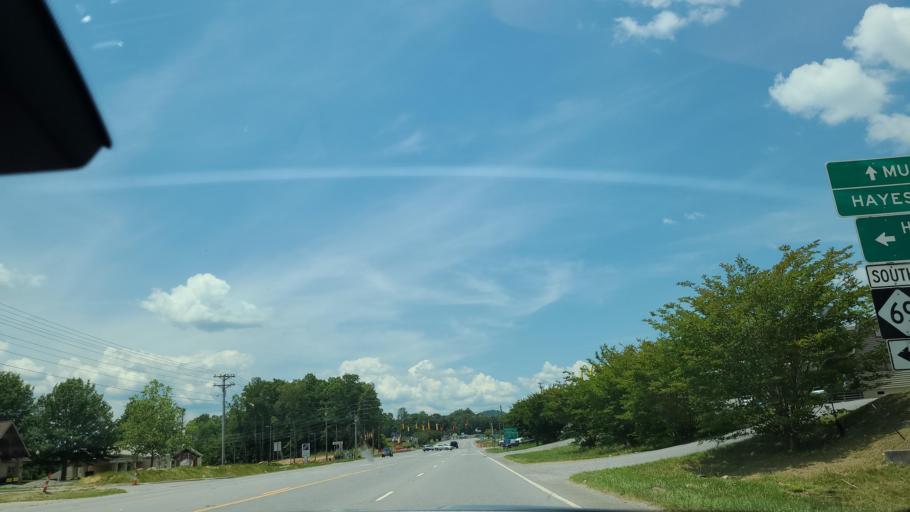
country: US
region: North Carolina
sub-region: Clay County
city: Hayesville
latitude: 35.0347
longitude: -83.8187
